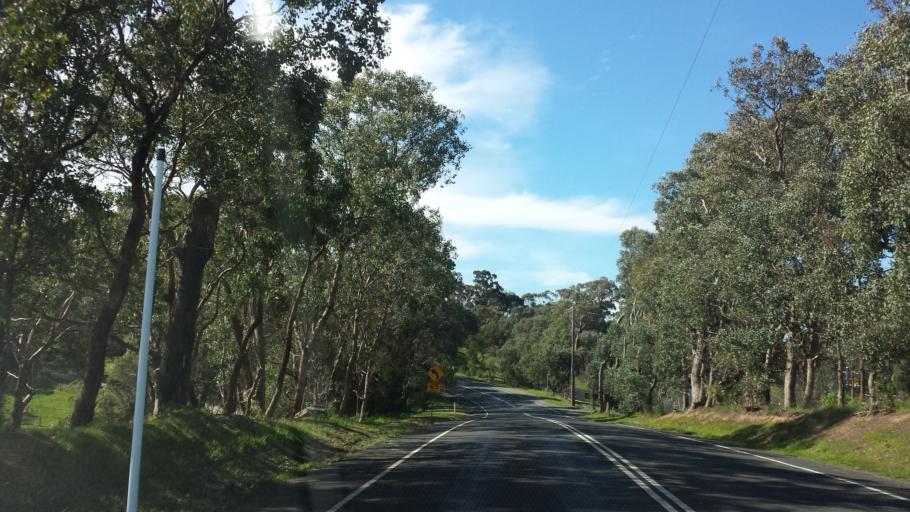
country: AU
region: Victoria
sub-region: Nillumbik
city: North Warrandyte
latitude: -37.7079
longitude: 145.2238
